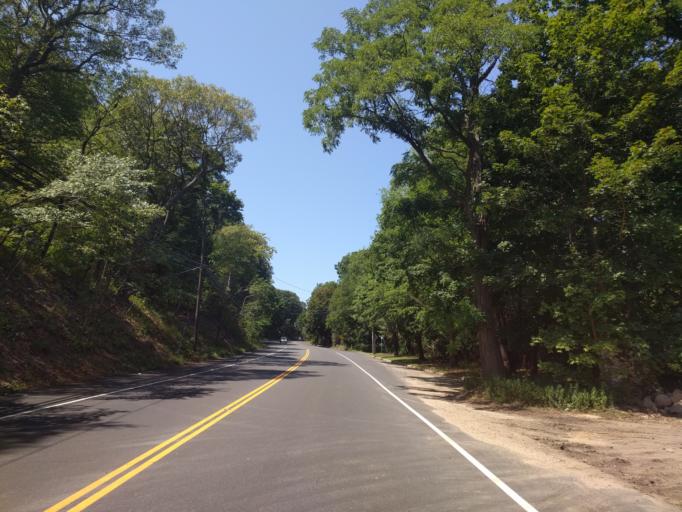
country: US
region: New York
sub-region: Suffolk County
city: Fort Salonga
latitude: 40.9122
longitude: -73.3026
